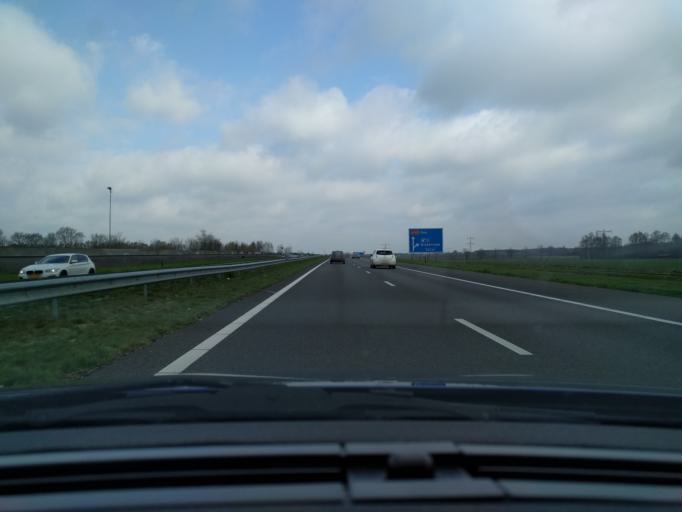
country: NL
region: North Brabant
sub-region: Gemeente Bernheze
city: Heesch
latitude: 51.7033
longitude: 5.5740
